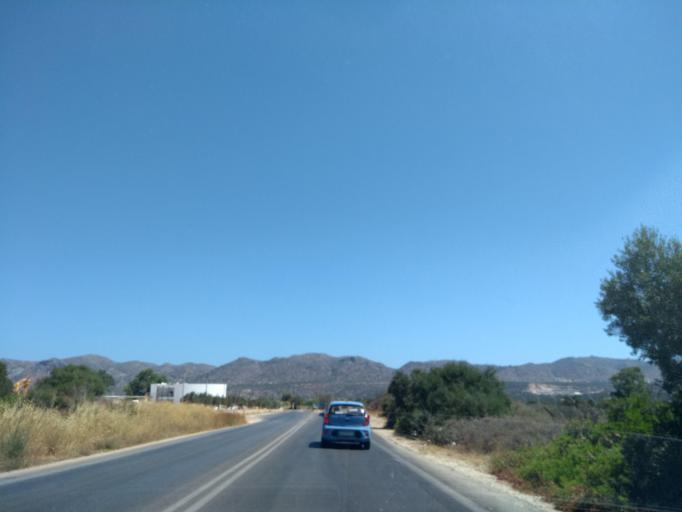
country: GR
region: Crete
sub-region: Nomos Chanias
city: Mouzouras
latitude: 35.5385
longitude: 24.1293
